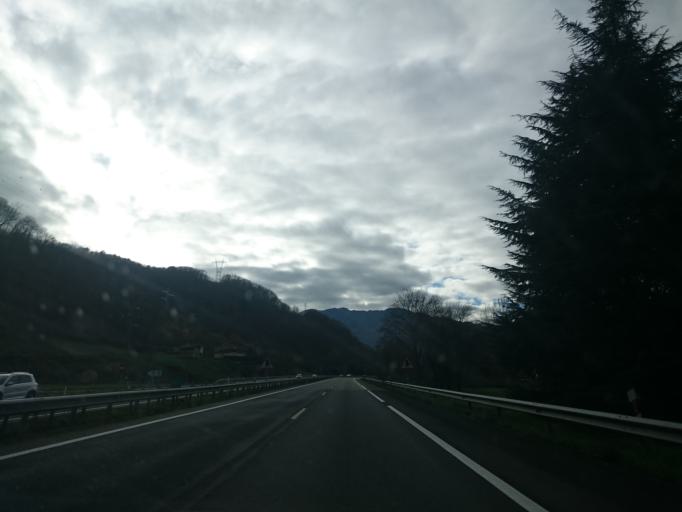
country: ES
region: Asturias
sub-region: Province of Asturias
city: Pola de Lena
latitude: 43.1818
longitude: -5.8106
